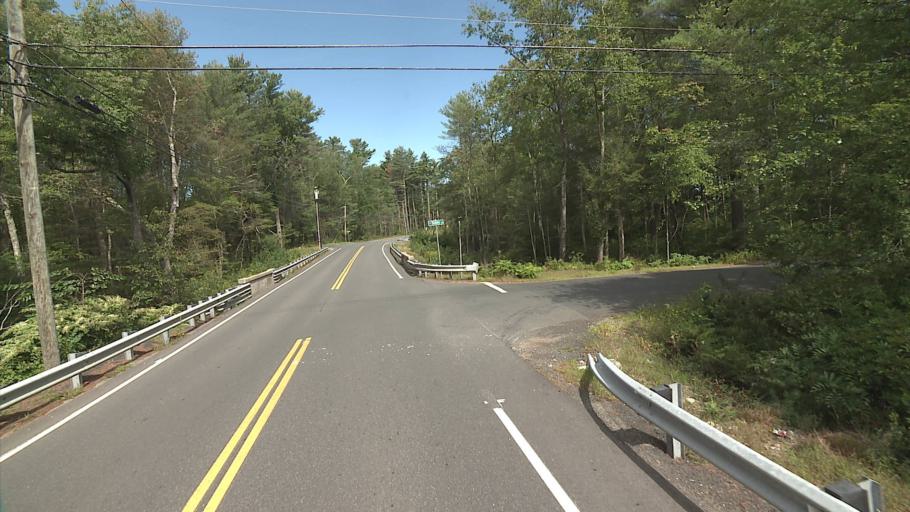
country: US
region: Connecticut
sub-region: Tolland County
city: Stafford
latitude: 42.0151
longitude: -72.3167
